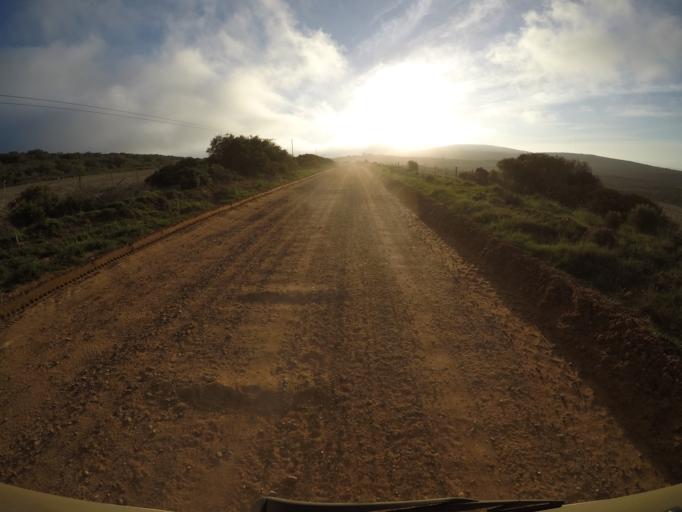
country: ZA
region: Western Cape
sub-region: Eden District Municipality
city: Mossel Bay
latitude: -34.1431
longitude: 22.0267
